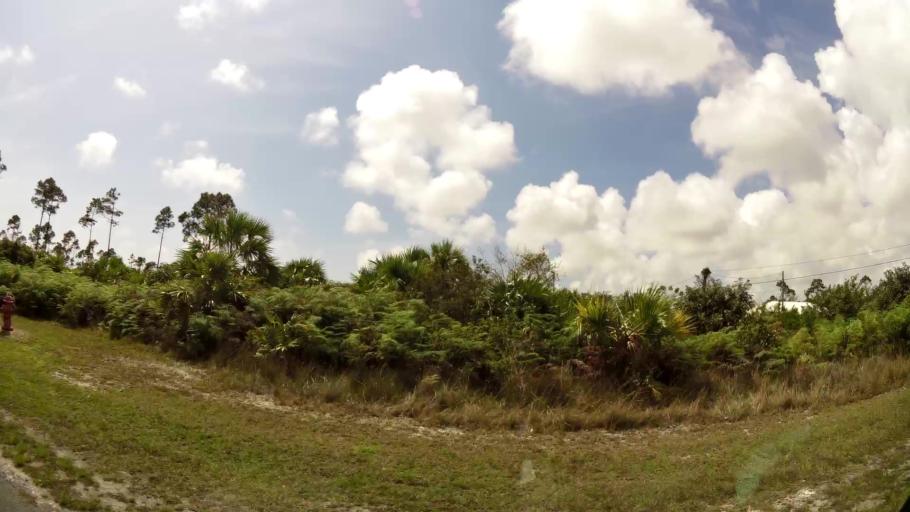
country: BS
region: Freeport
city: Freeport
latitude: 26.5158
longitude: -78.7225
